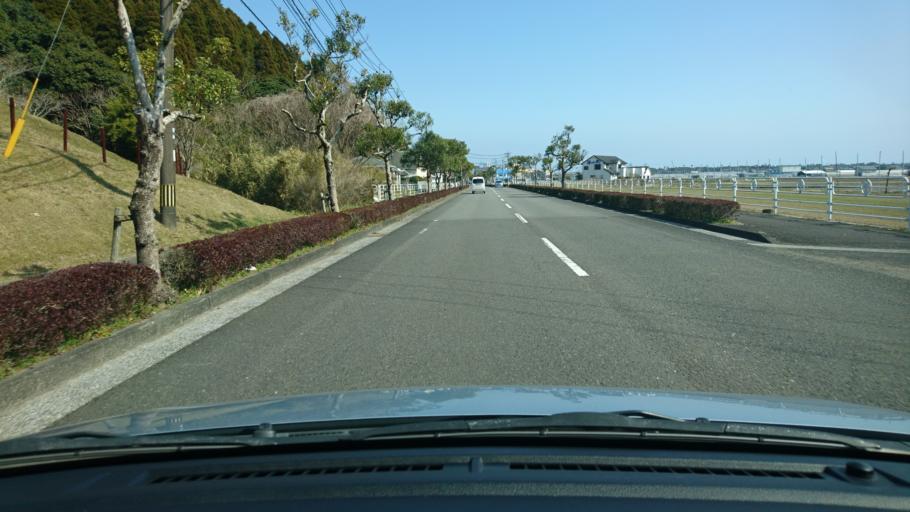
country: JP
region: Miyazaki
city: Miyazaki-shi
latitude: 31.8267
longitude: 131.4312
